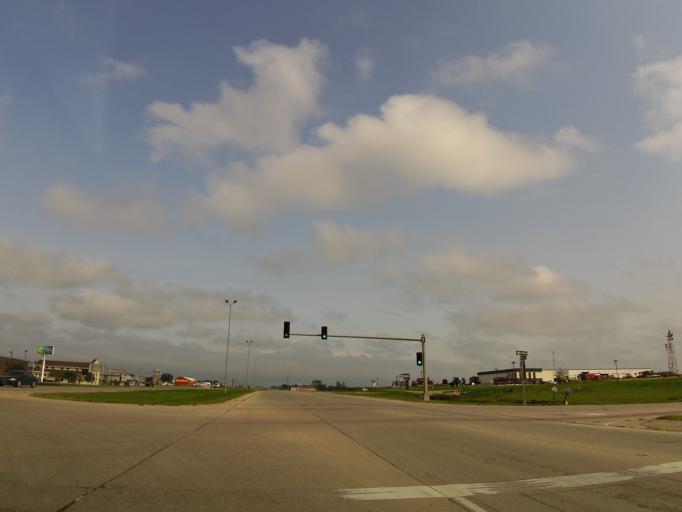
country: US
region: South Dakota
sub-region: Codington County
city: Watertown
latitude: 44.8900
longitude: -97.0557
